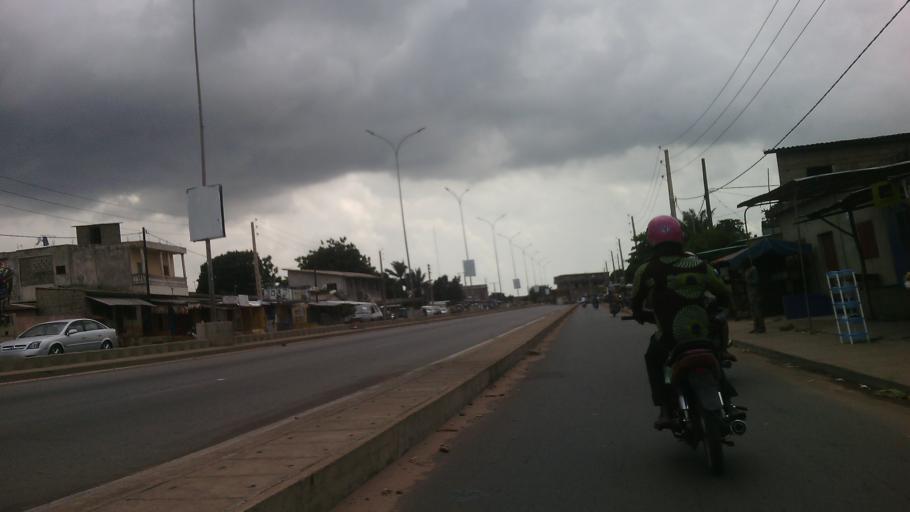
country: BJ
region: Atlantique
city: Abomey-Calavi
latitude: 6.4507
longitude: 2.3564
